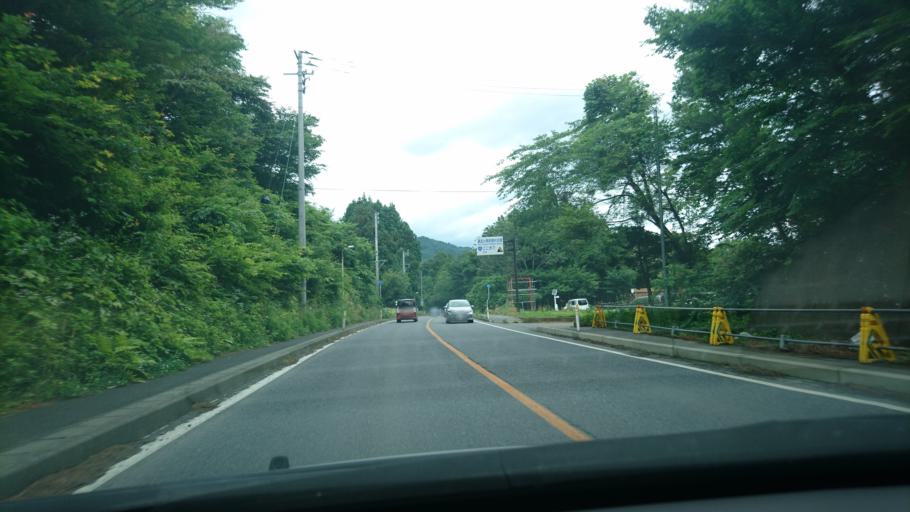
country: JP
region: Iwate
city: Otsuchi
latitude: 39.3767
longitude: 141.9413
